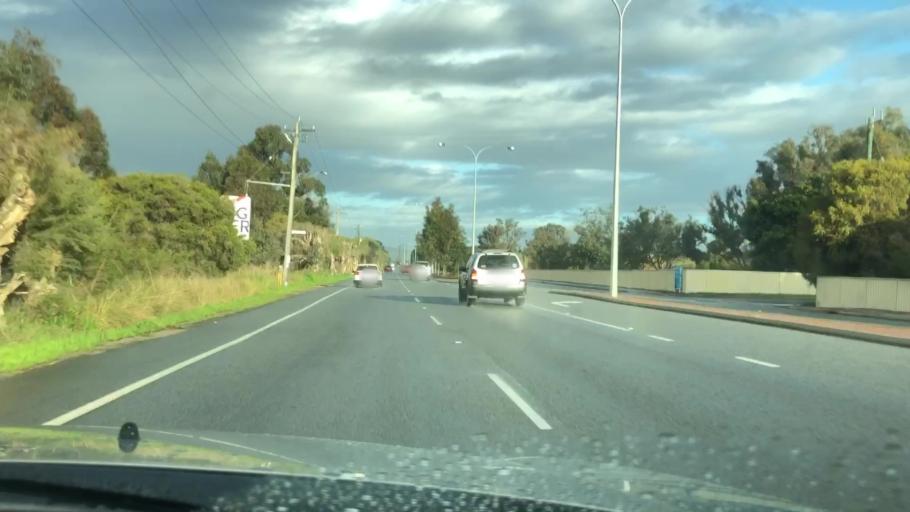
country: AU
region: Western Australia
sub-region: Armadale
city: Harrisdale
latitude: -32.1102
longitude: 115.9420
